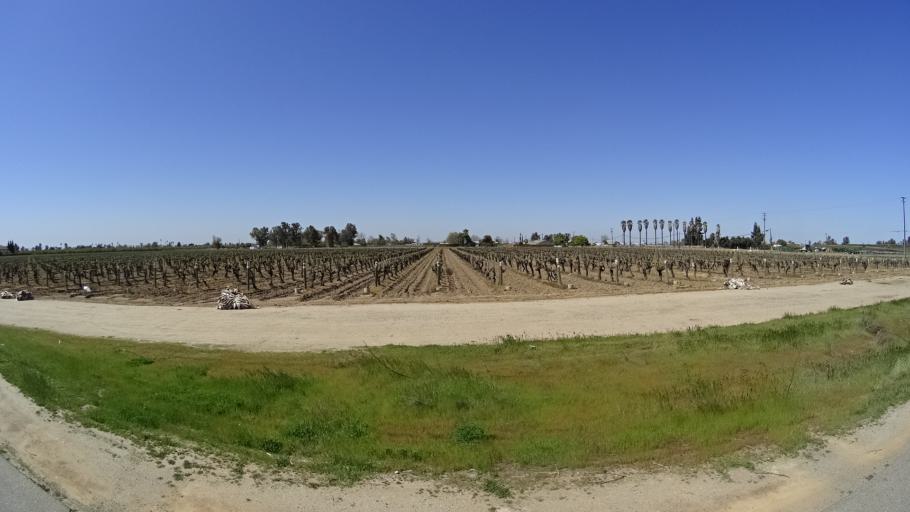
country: US
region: California
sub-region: Fresno County
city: West Park
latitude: 36.7347
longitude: -119.8444
